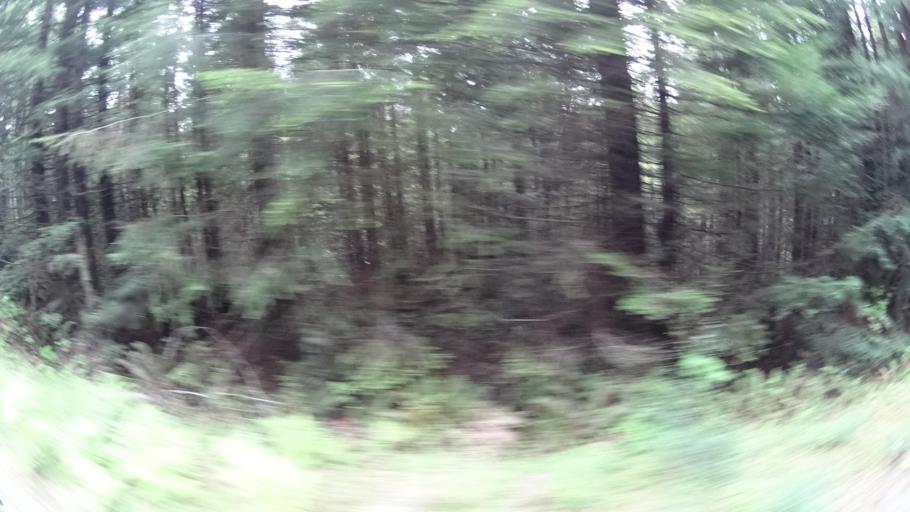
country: US
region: California
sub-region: Humboldt County
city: Blue Lake
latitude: 40.8775
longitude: -123.9693
